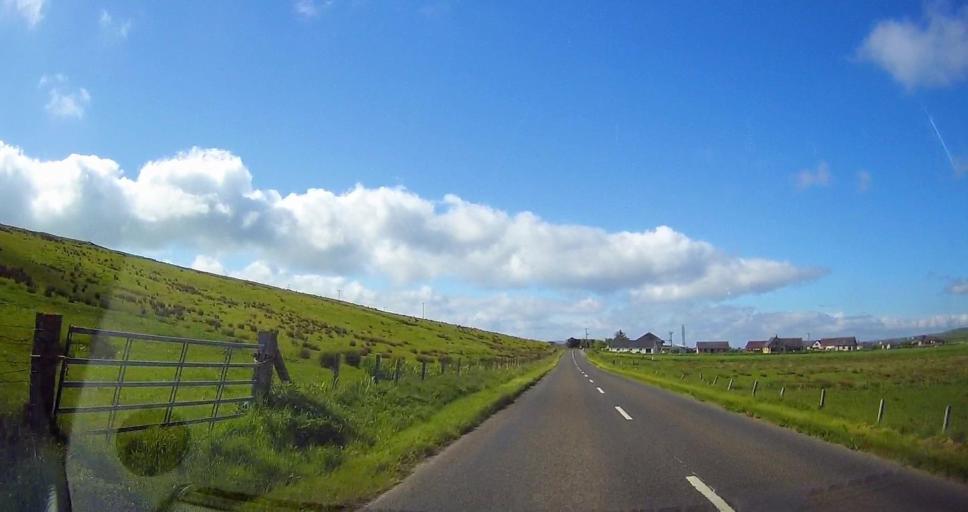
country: GB
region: Scotland
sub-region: Orkney Islands
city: Orkney
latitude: 58.9646
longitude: -2.9664
